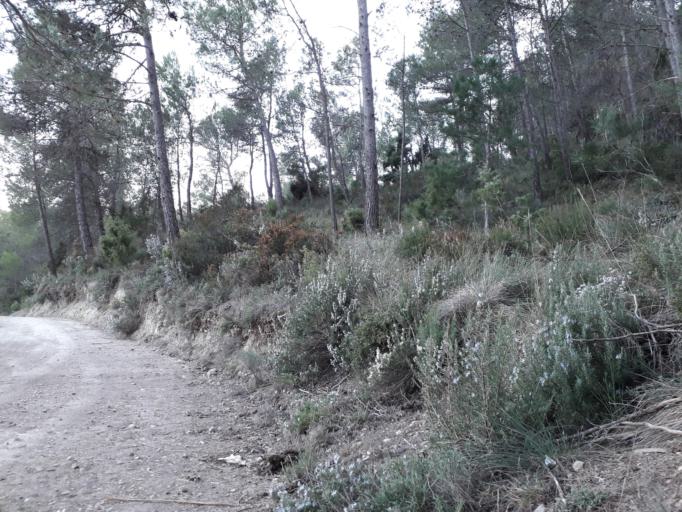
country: ES
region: Catalonia
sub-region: Provincia de Barcelona
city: Sant Marti de Tous
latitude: 41.5234
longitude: 1.5143
